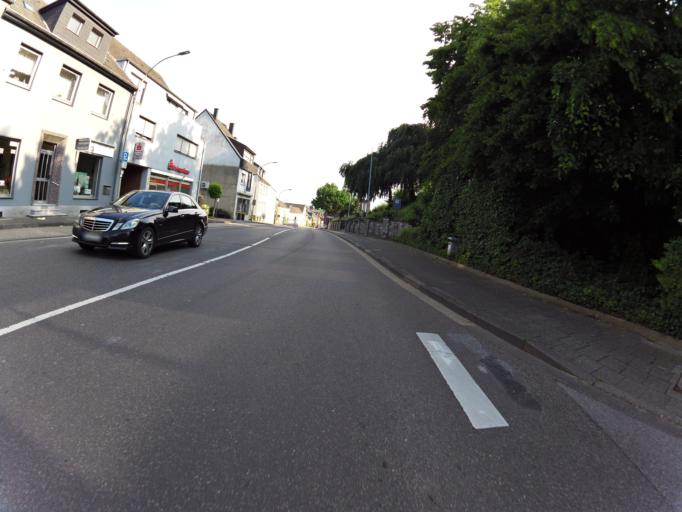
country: DE
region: North Rhine-Westphalia
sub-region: Regierungsbezirk Koln
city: Ubach-Palenberg
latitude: 50.9420
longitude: 6.1058
